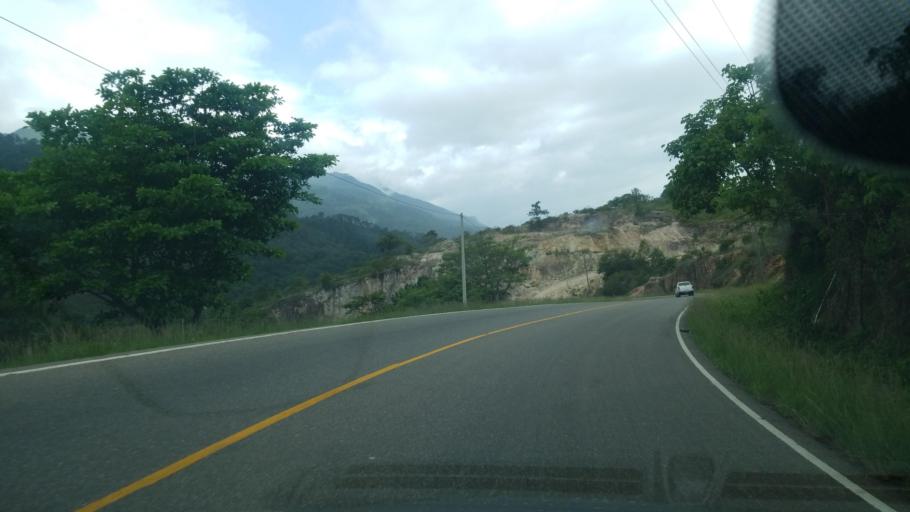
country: HN
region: Ocotepeque
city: Sinuapa
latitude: 14.4554
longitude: -89.1701
